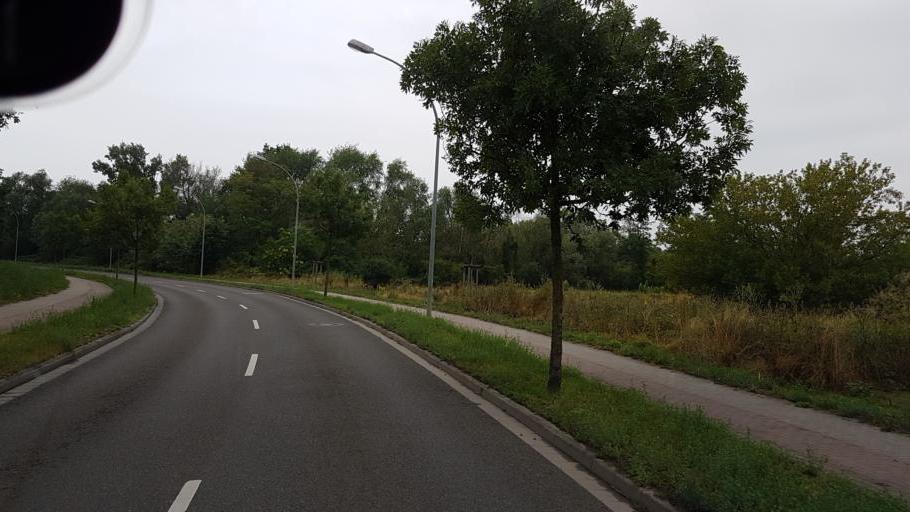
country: DE
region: Rheinland-Pfalz
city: Speyer
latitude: 49.3379
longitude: 8.4367
